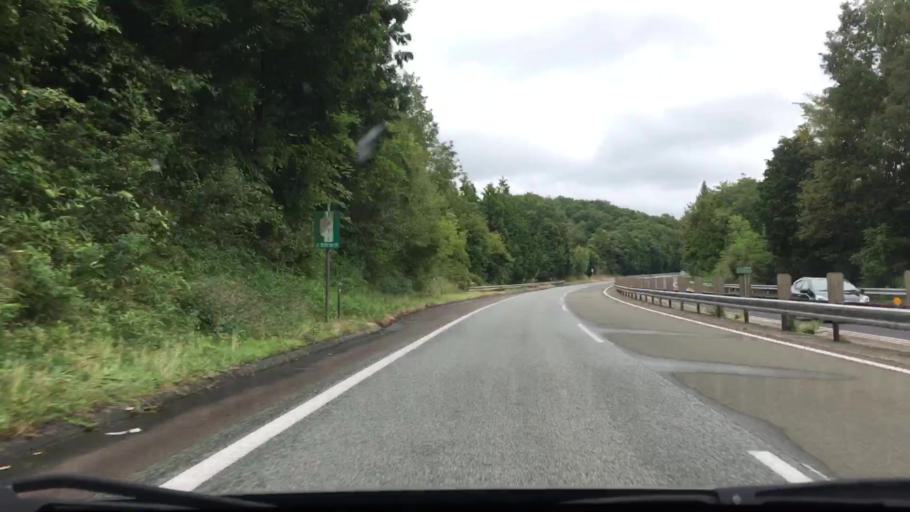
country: JP
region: Hiroshima
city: Miyoshi
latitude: 34.7899
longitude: 132.8801
